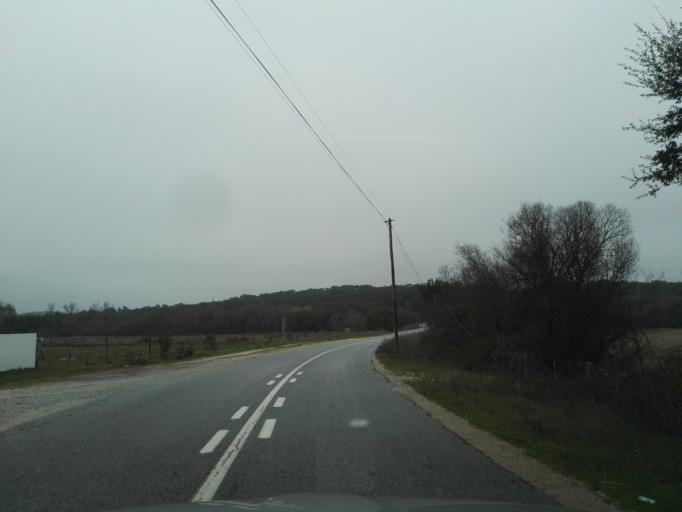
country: PT
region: Evora
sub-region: Vendas Novas
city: Vendas Novas
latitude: 38.7617
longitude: -8.4219
